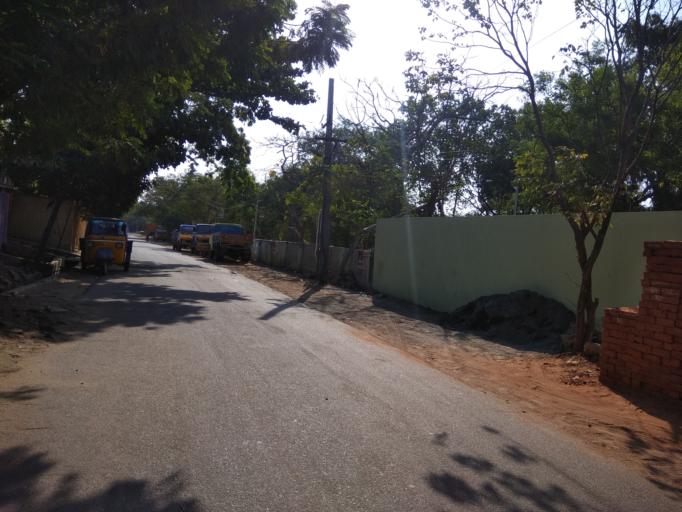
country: IN
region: Tamil Nadu
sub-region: Kancheepuram
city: Saint Thomas Mount
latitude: 13.0093
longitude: 80.1956
